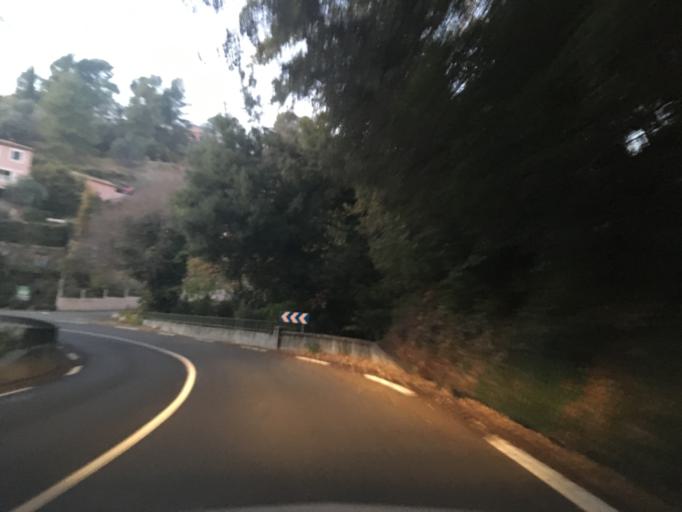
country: FR
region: Provence-Alpes-Cote d'Azur
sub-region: Departement du Var
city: Draguignan
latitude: 43.5379
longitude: 6.4846
